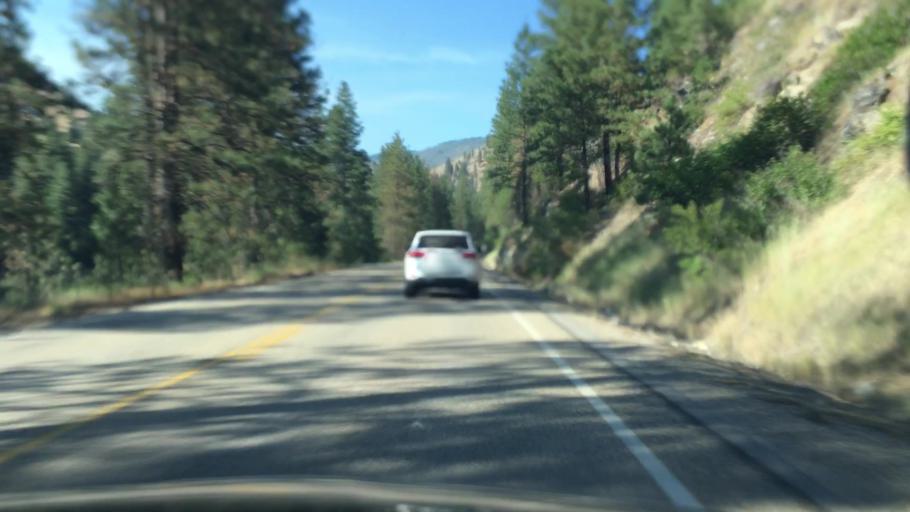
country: US
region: Idaho
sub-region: Boise County
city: Idaho City
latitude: 44.0575
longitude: -116.1268
